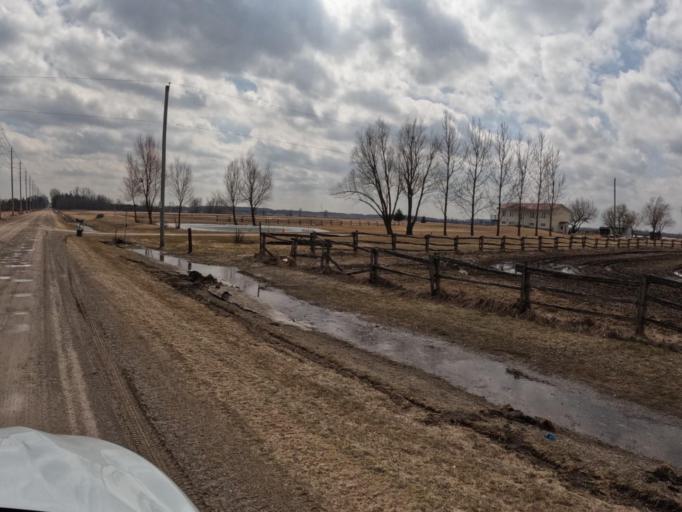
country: CA
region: Ontario
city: Shelburne
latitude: 44.0269
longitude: -80.3144
